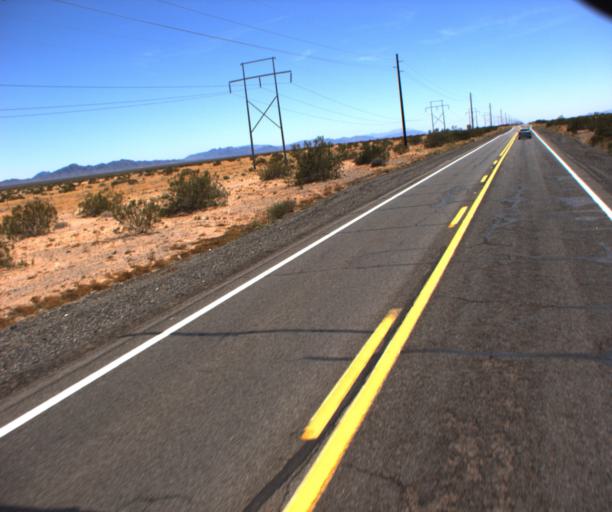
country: US
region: Arizona
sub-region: La Paz County
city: Parker
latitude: 33.9465
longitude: -114.2169
